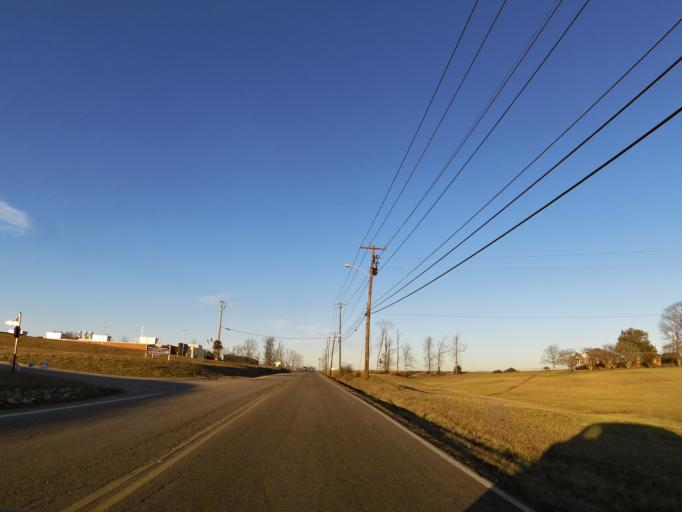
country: US
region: Tennessee
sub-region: Knox County
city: Mascot
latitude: 35.9931
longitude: -83.7849
